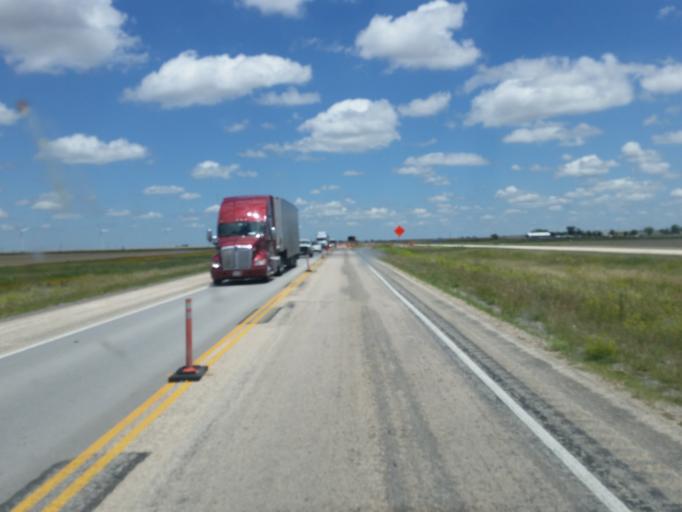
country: US
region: Texas
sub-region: Nolan County
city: Roscoe
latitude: 32.4538
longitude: -100.5489
